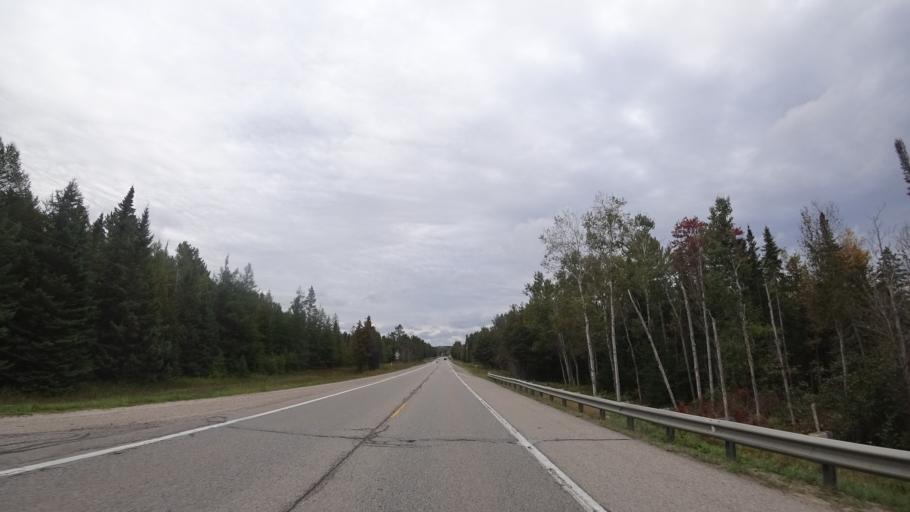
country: US
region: Michigan
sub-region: Charlevoix County
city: Boyne City
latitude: 45.1824
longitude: -84.9145
